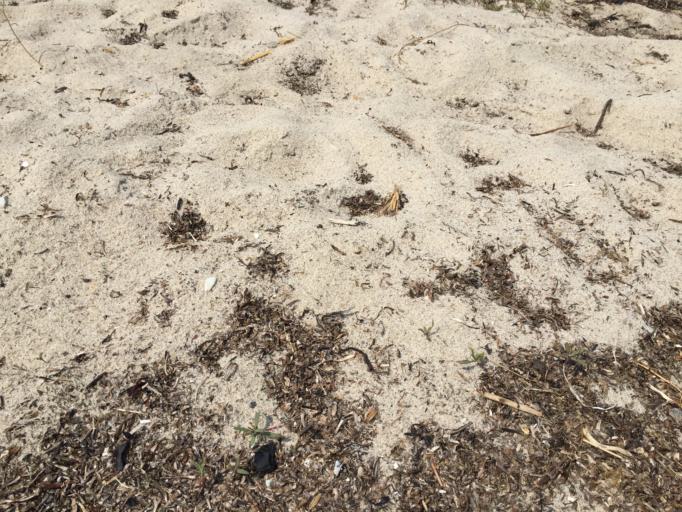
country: DK
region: South Denmark
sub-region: Langeland Kommune
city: Rudkobing
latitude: 54.9819
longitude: 10.7892
